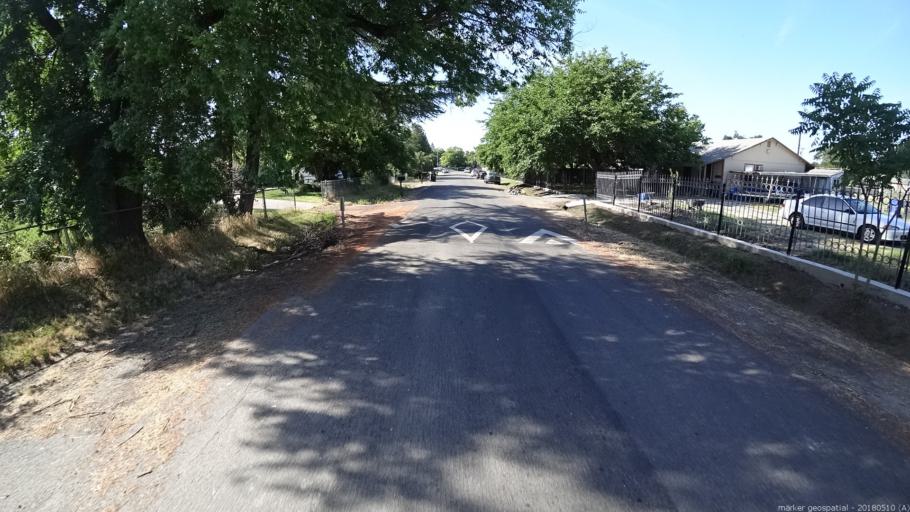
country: US
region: California
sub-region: Sacramento County
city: Rio Linda
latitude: 38.6578
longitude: -121.4802
